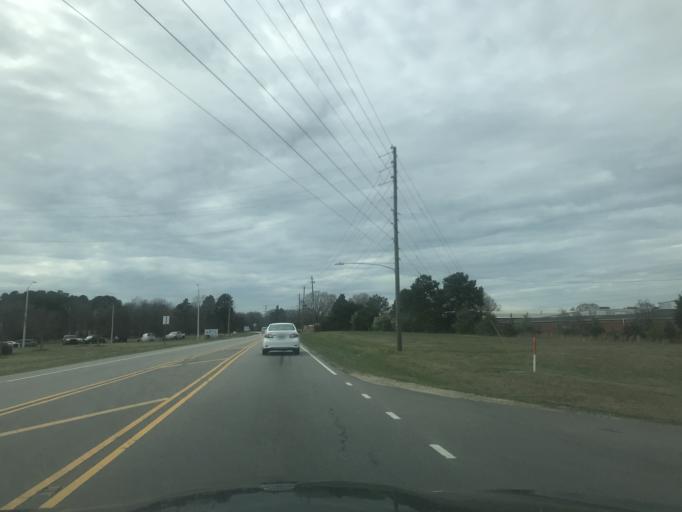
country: US
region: North Carolina
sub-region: Franklin County
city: Louisburg
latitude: 36.0855
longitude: -78.3189
